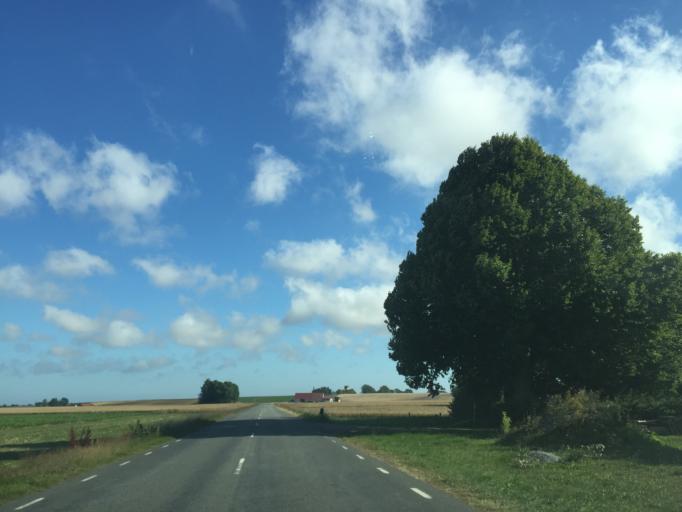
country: SE
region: Skane
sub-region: Ystads Kommun
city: Kopingebro
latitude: 55.4528
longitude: 14.1155
